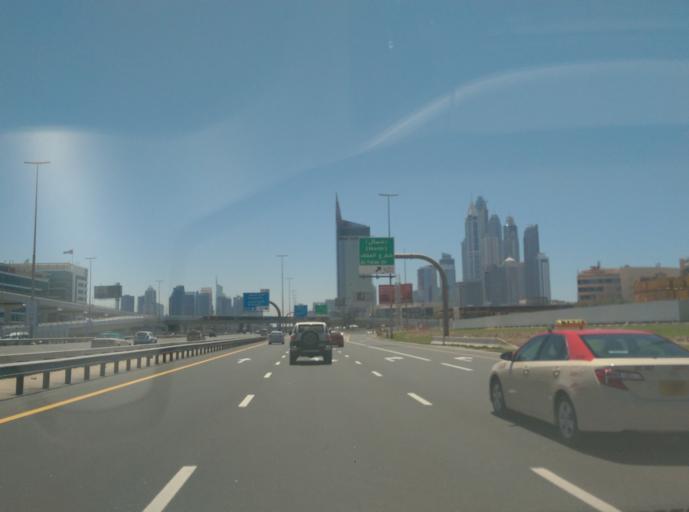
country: AE
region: Dubai
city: Dubai
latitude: 25.0979
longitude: 55.1674
